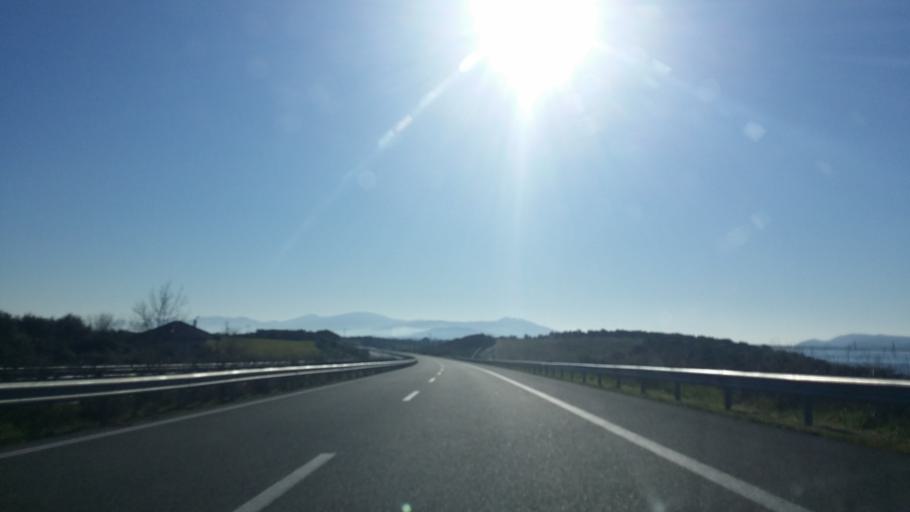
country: GR
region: West Greece
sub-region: Nomos Aitolias kai Akarnanias
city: Fitiai
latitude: 38.6790
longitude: 21.2199
